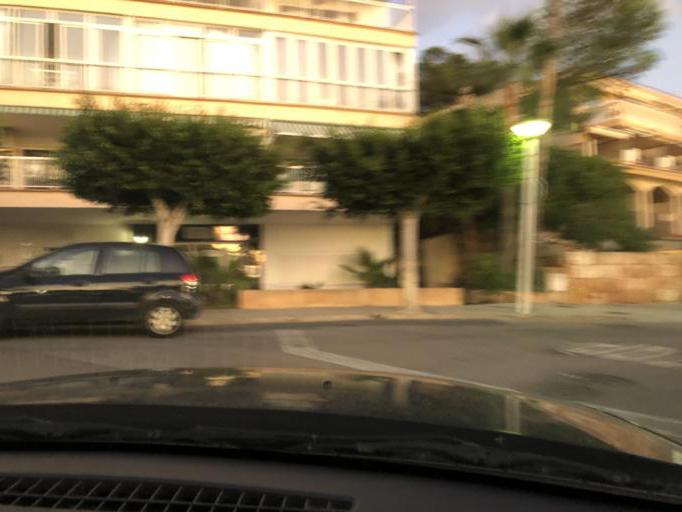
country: ES
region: Balearic Islands
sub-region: Illes Balears
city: Santa Ponsa
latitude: 39.5204
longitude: 2.4733
